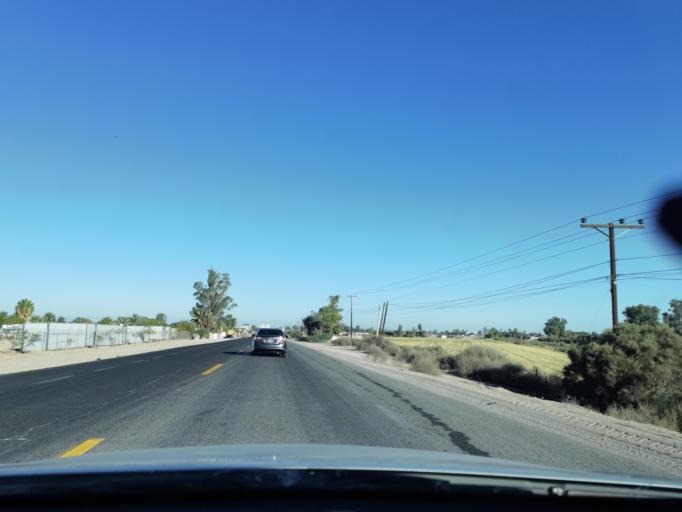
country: MX
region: Baja California
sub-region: Mexicali
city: Islas Agrarias Grupo A
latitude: 32.6457
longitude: -115.3208
